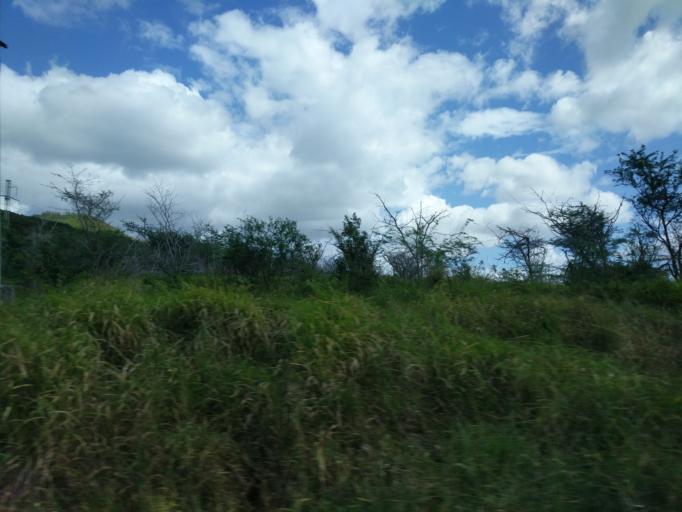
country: PR
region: Santa Isabel Municipio
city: El Ojo
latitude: 18.0206
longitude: -66.3701
